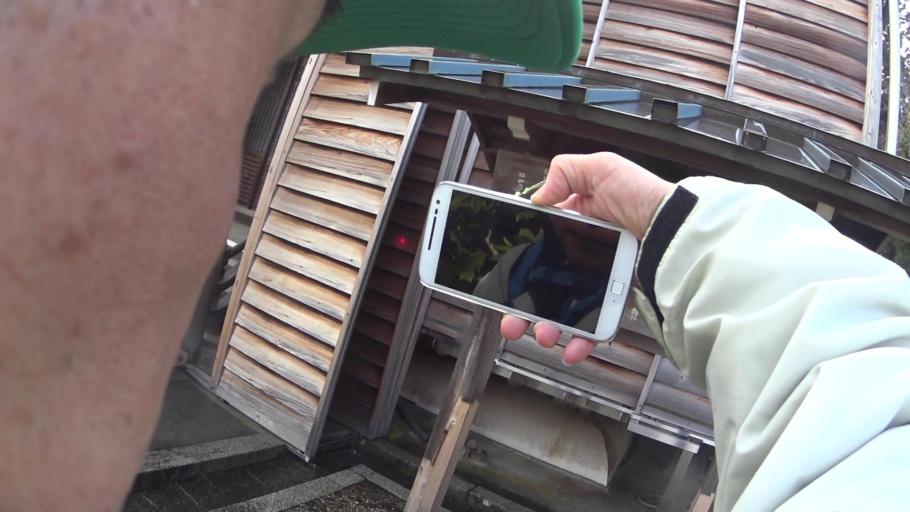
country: JP
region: Kyoto
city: Muko
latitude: 34.9394
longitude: 135.6437
